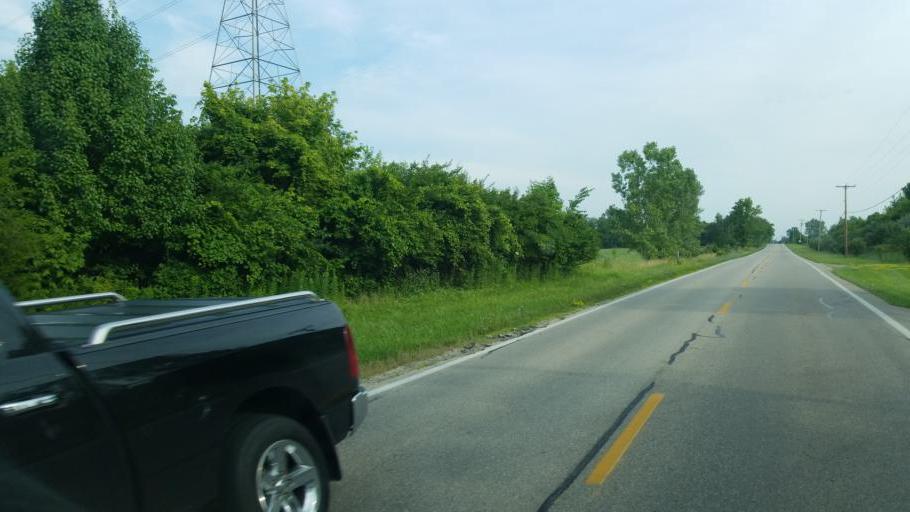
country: US
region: Ohio
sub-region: Delaware County
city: Powell
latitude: 40.1779
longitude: -83.1381
